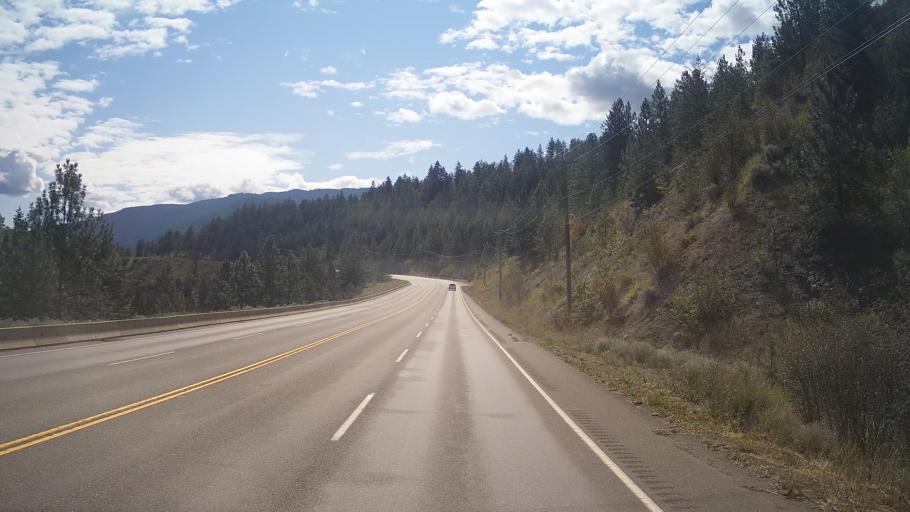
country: CA
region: British Columbia
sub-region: Thompson-Nicola Regional District
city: Ashcroft
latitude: 50.2558
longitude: -121.5217
